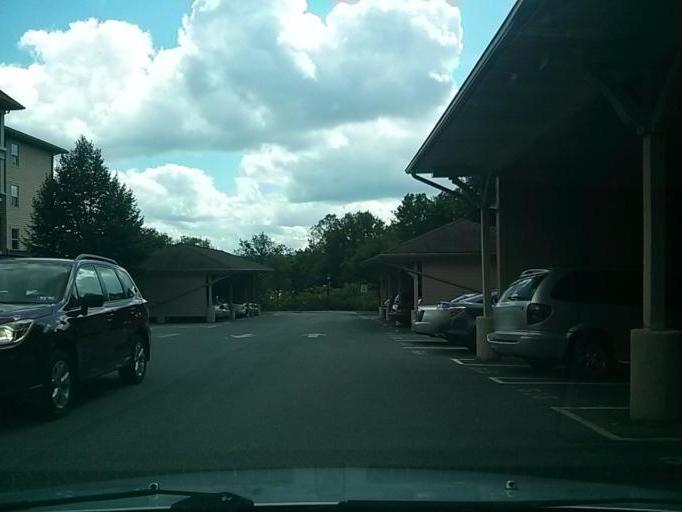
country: US
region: Pennsylvania
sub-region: Centre County
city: State College
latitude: 40.8235
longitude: -77.8754
